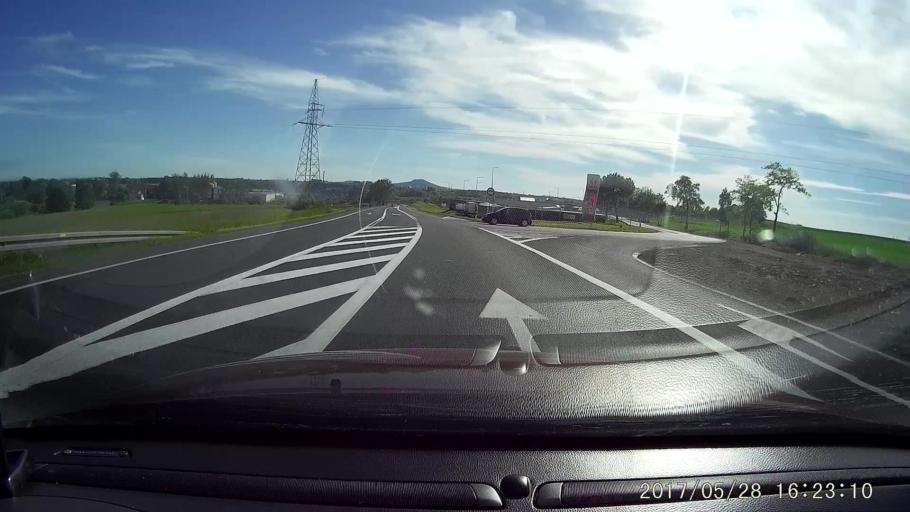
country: PL
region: Lower Silesian Voivodeship
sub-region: Powiat zgorzelecki
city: Lagow
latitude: 51.1823
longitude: 15.0376
